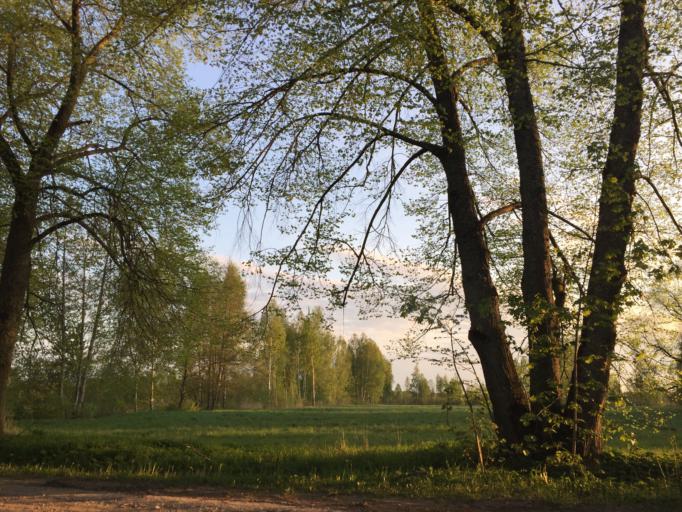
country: LV
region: Jurmala
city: Jurmala
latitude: 56.9036
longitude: 23.7353
